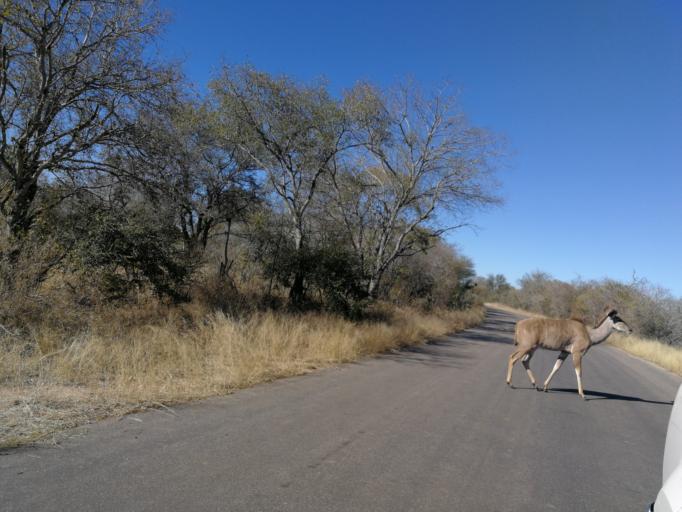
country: ZA
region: Mpumalanga
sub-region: Ehlanzeni District
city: Komatipoort
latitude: -24.9665
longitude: 31.6838
